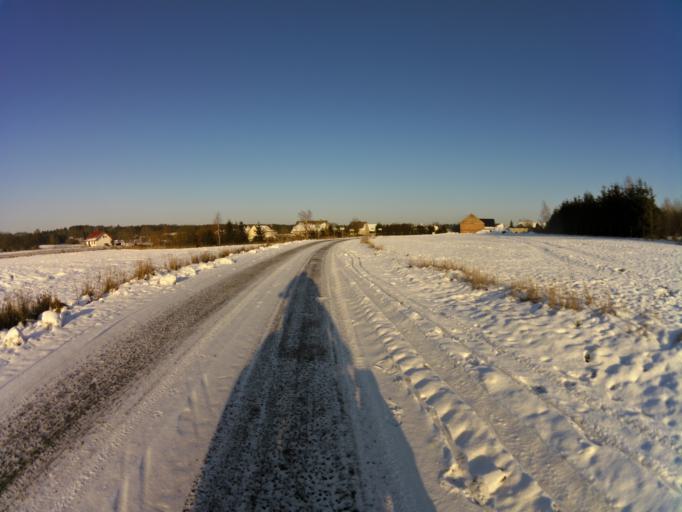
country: PL
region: West Pomeranian Voivodeship
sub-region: Powiat stargardzki
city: Dobrzany
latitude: 53.3266
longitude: 15.4385
